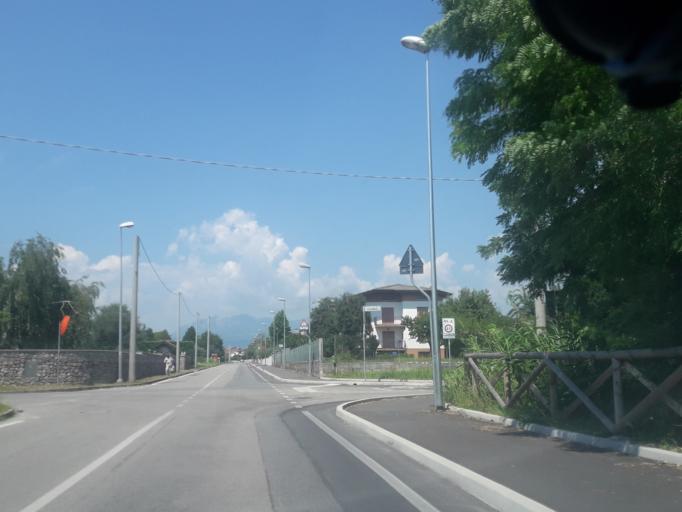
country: IT
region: Friuli Venezia Giulia
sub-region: Provincia di Udine
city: Pagnacco
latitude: 46.1035
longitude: 13.1833
